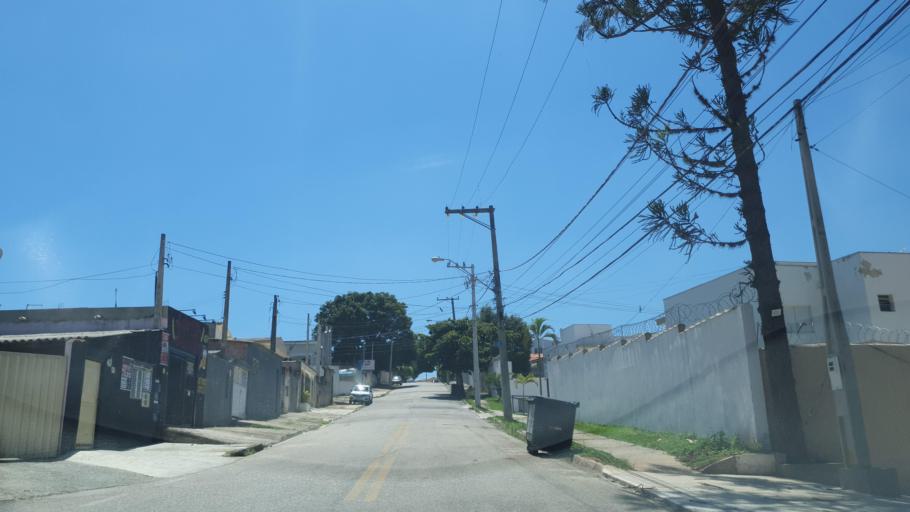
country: BR
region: Sao Paulo
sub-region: Sorocaba
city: Sorocaba
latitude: -23.4725
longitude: -47.5084
